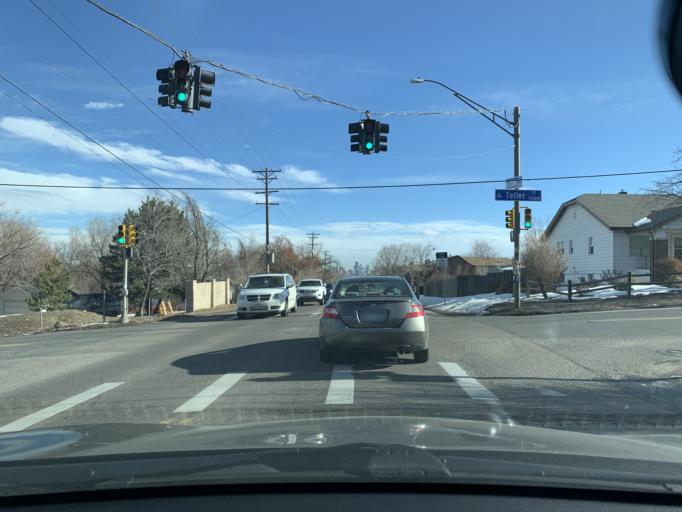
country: US
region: Colorado
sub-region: Jefferson County
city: Edgewater
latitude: 39.7473
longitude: -105.0762
